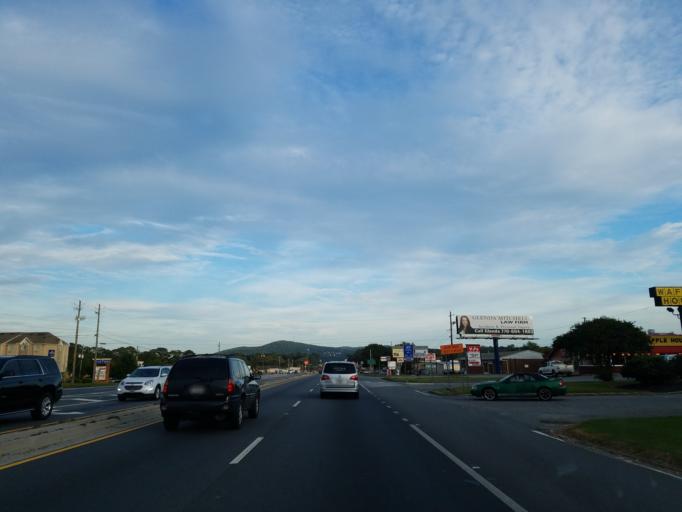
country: US
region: Georgia
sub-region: Bartow County
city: Cartersville
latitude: 34.2068
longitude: -84.8189
